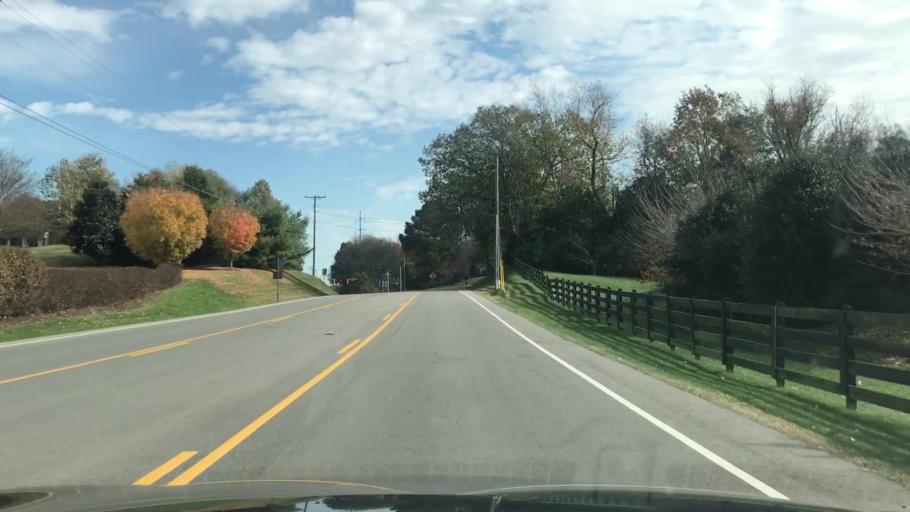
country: US
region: Tennessee
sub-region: Williamson County
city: Franklin
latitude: 35.9173
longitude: -86.7938
